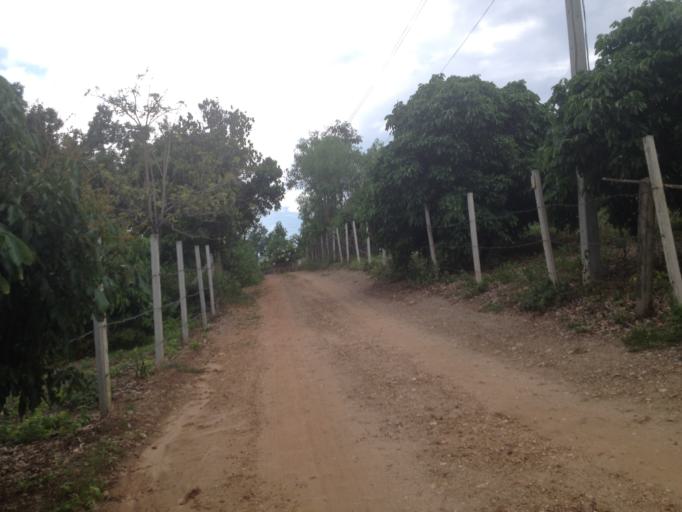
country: TH
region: Chiang Mai
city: Hang Dong
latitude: 18.6939
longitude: 98.8818
